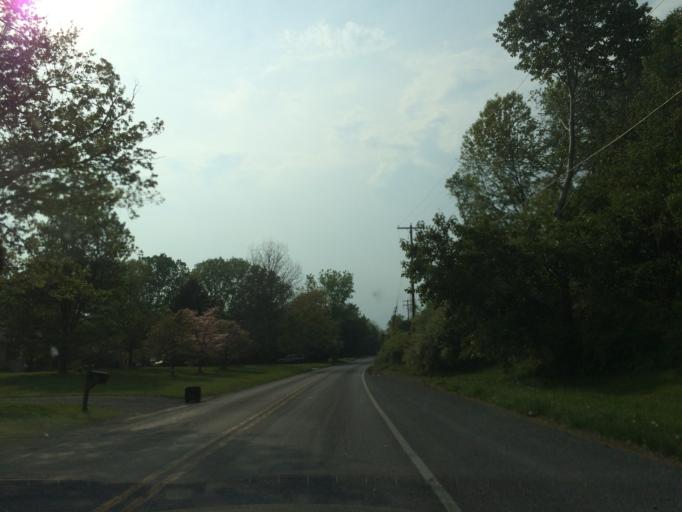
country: US
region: Maryland
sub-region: Carroll County
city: Mount Airy
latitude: 39.3502
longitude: -77.0780
